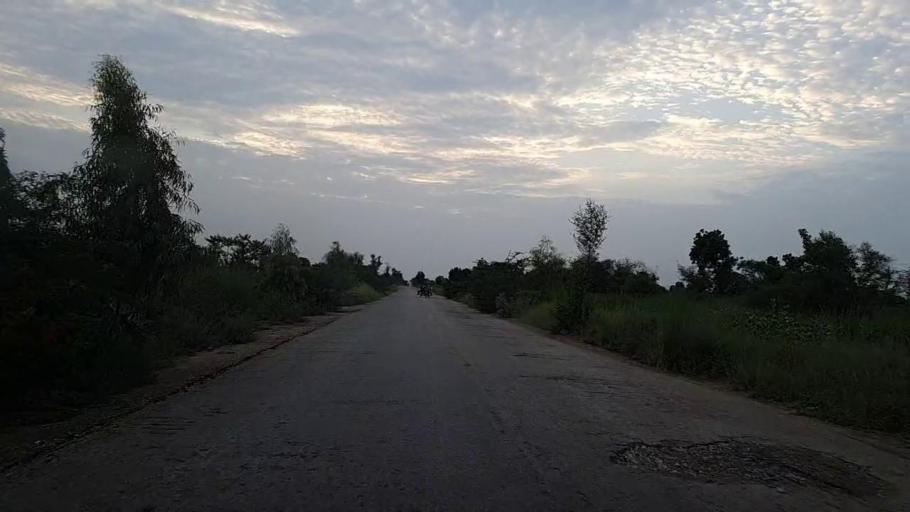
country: PK
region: Sindh
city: Naushahro Firoz
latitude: 26.8187
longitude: 68.1738
